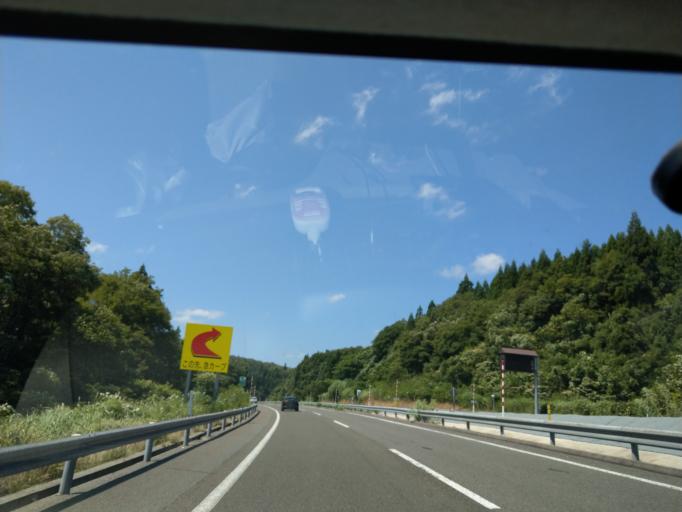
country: JP
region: Akita
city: Akita
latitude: 39.5792
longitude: 140.2938
